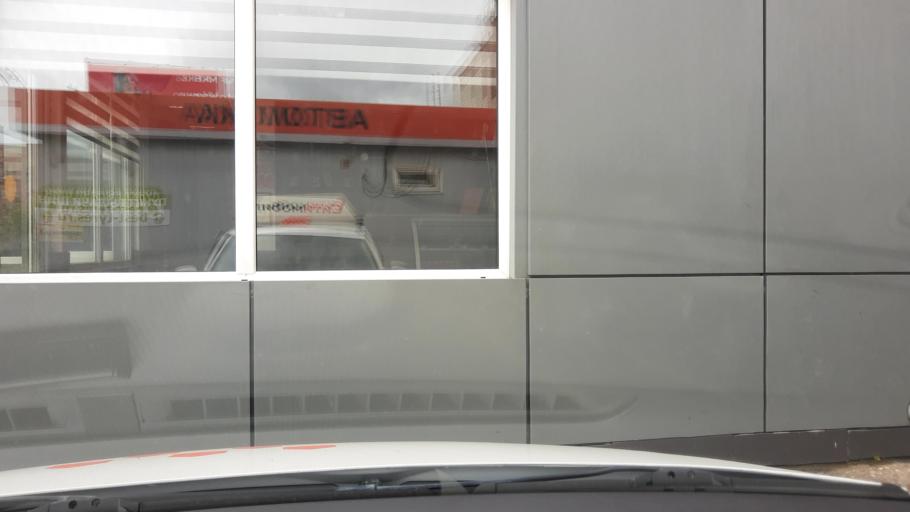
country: RU
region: Moskovskaya
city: Elektrostal'
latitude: 55.7749
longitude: 38.4258
